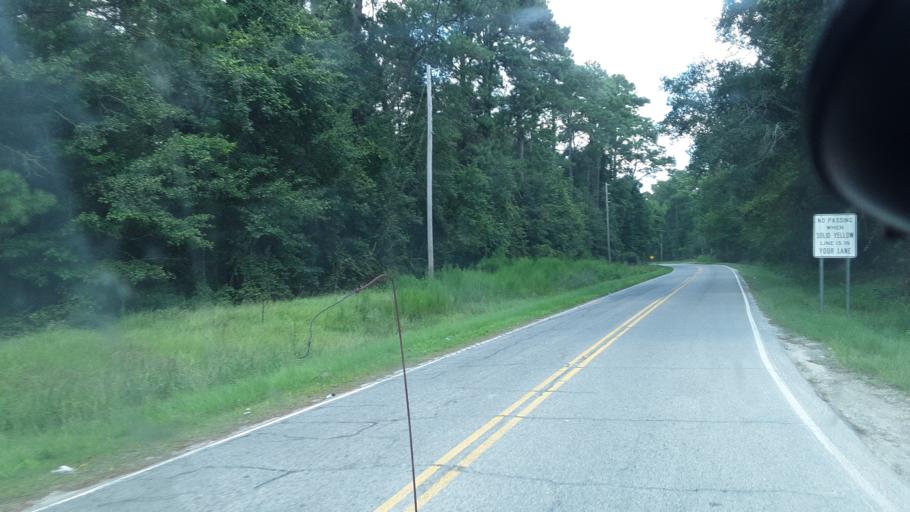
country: US
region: South Carolina
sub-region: Florence County
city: Johnsonville
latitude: 33.6593
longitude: -79.4189
